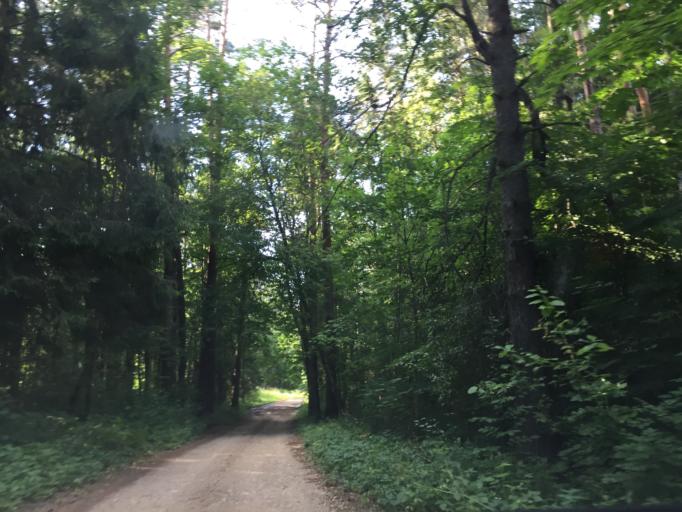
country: LV
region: Krimulda
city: Ragana
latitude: 57.1365
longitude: 24.7687
